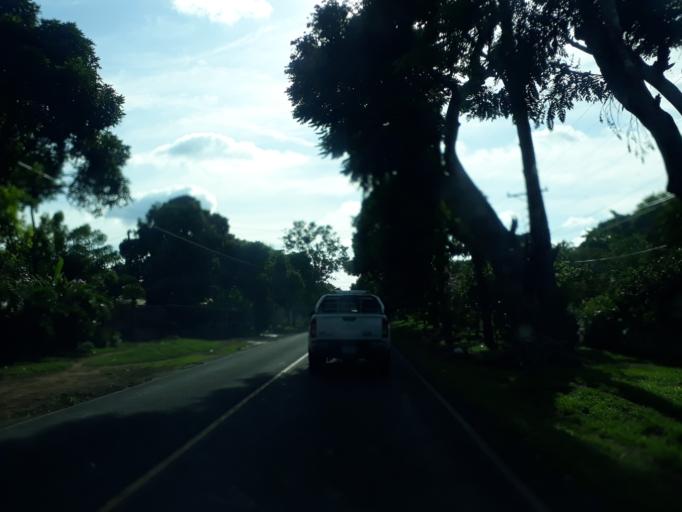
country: NI
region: Carazo
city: San Marcos
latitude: 11.9051
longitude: -86.1743
